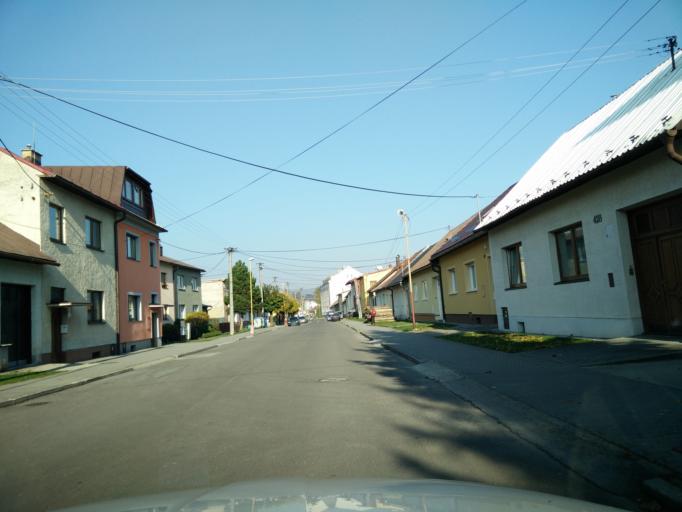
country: SK
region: Zilinsky
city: Rajec
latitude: 49.0865
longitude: 18.6413
